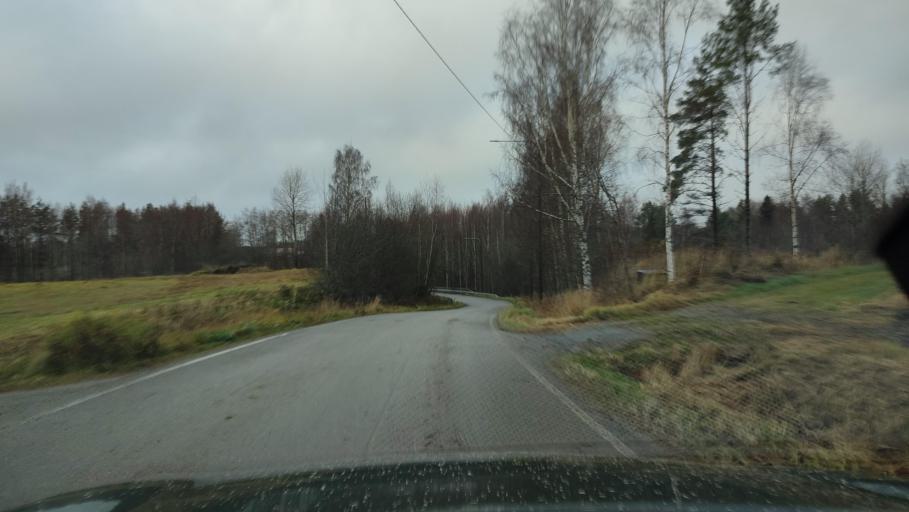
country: FI
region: Southern Ostrobothnia
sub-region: Suupohja
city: Teuva
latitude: 62.4486
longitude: 21.6080
